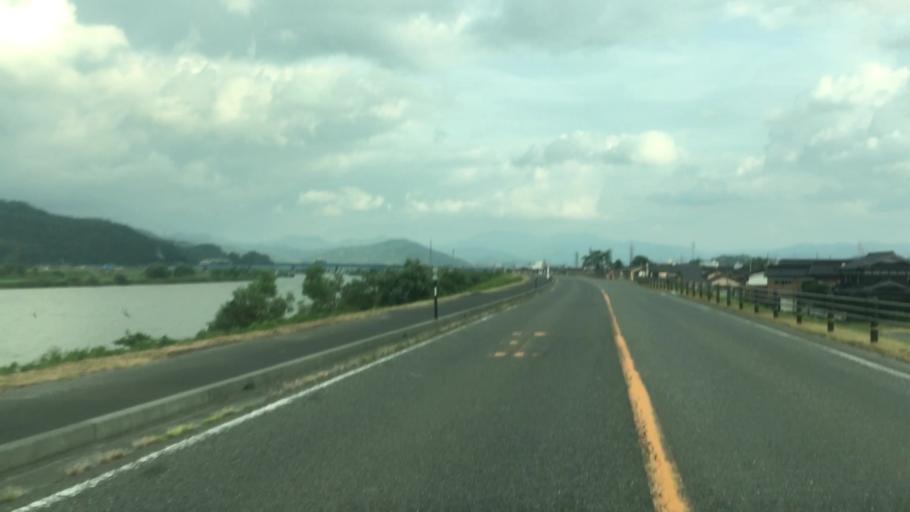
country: JP
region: Hyogo
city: Toyooka
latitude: 35.5637
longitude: 134.8124
